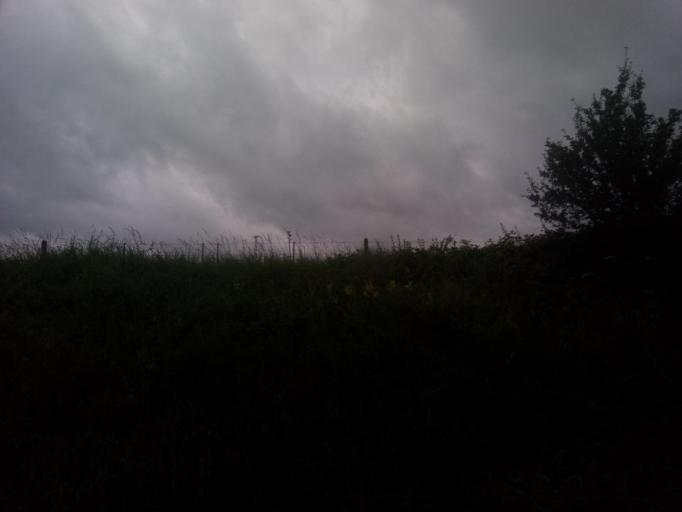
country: GB
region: England
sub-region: North Yorkshire
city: Settle
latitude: 54.0250
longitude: -2.2692
